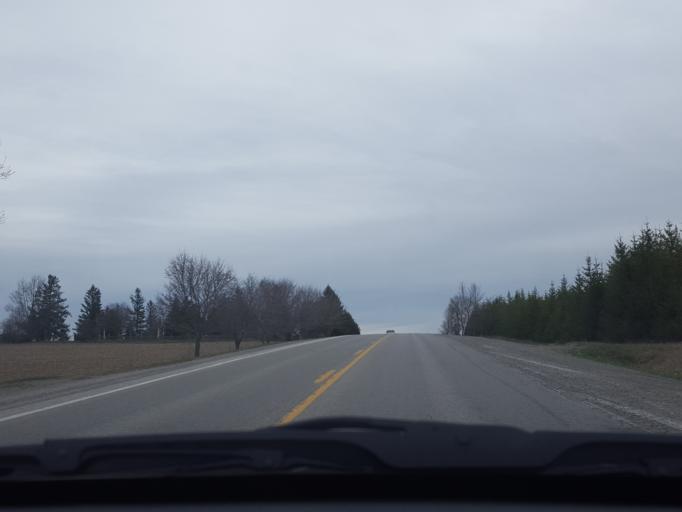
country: CA
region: Ontario
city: Uxbridge
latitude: 44.2406
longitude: -79.1270
